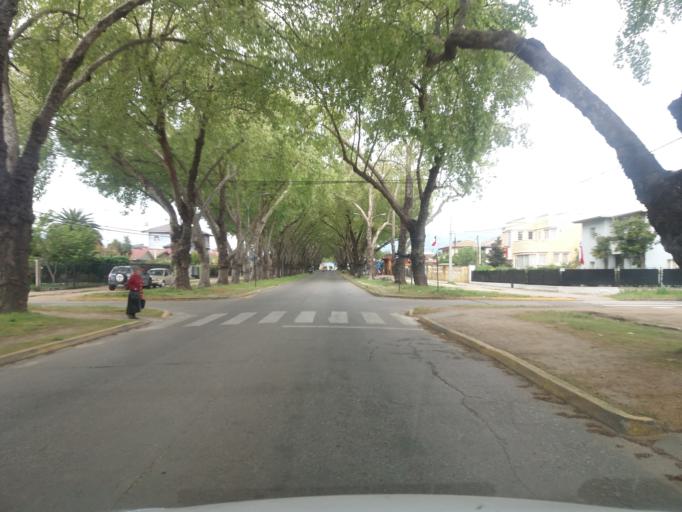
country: CL
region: Valparaiso
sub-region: Provincia de Marga Marga
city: Limache
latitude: -32.9887
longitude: -71.2680
